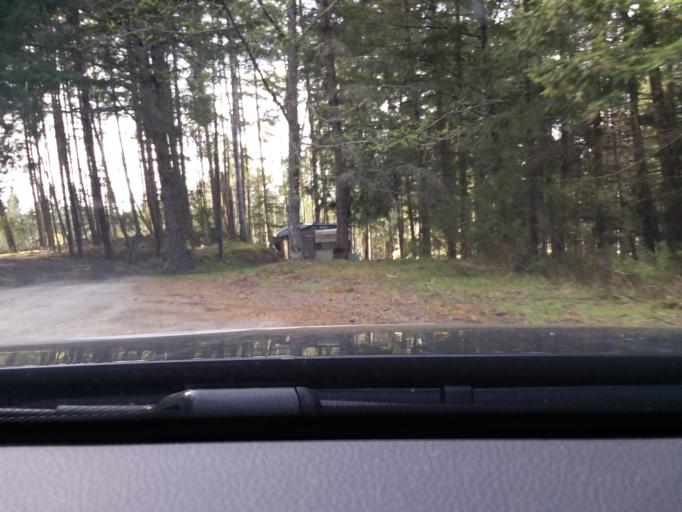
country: CA
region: British Columbia
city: North Saanich
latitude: 48.7706
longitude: -123.2970
